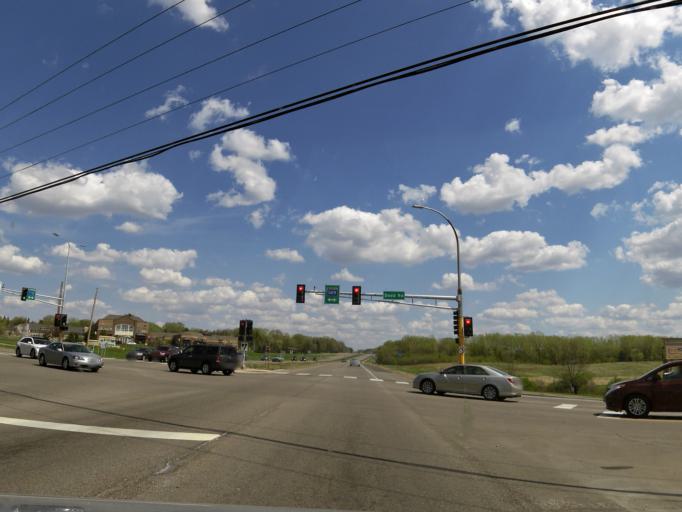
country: US
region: Minnesota
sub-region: Dakota County
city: Mendota Heights
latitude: 44.8836
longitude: -93.1250
